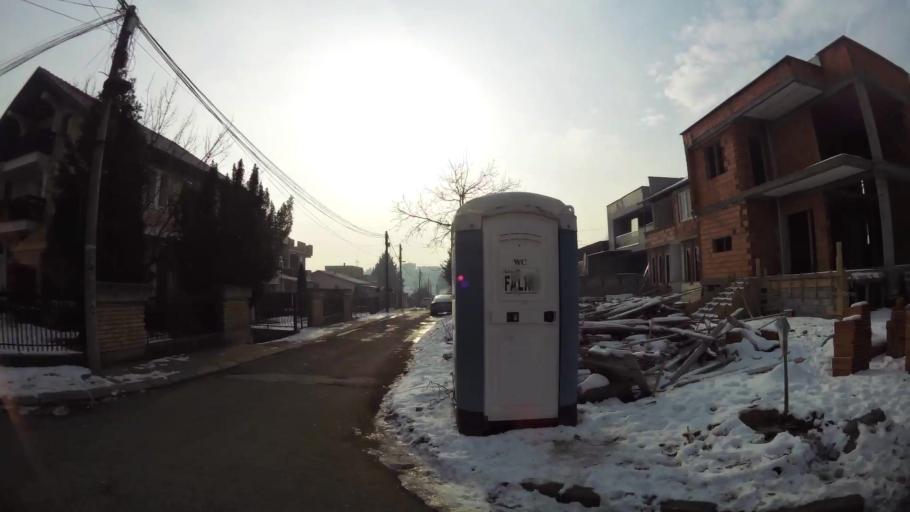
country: MK
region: Cair
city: Cair
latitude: 42.0198
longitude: 21.4525
